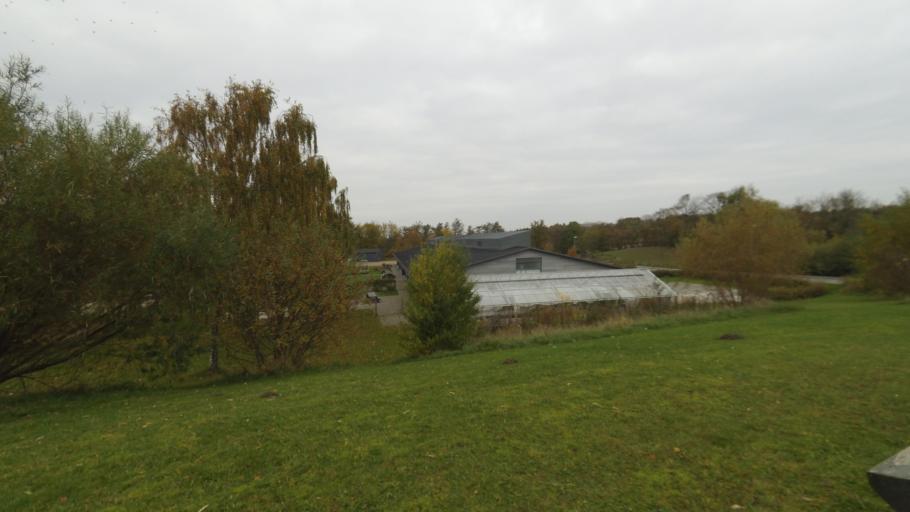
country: DK
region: Central Jutland
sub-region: Arhus Kommune
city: Stavtrup
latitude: 56.1178
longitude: 10.1317
